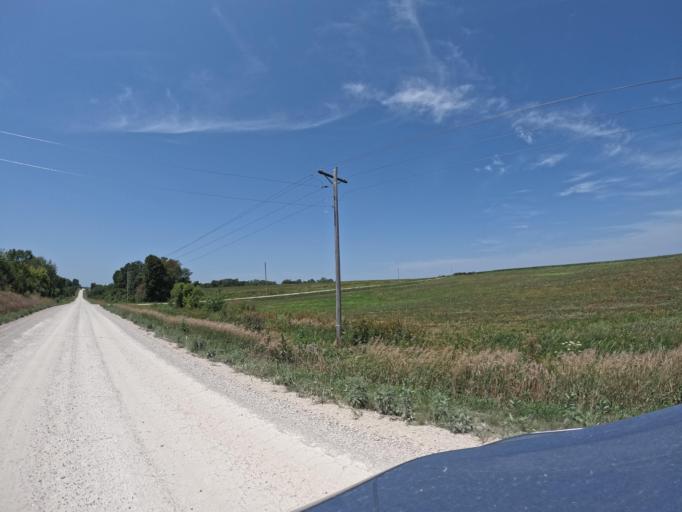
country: US
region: Iowa
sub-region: Henry County
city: Mount Pleasant
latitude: 40.9085
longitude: -91.6540
